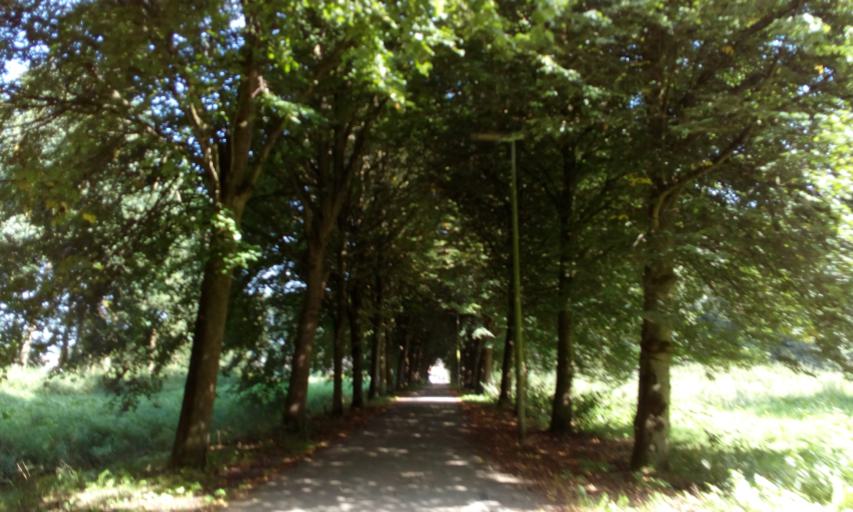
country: NL
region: South Holland
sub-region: Gemeente Waddinxveen
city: Groenswaard
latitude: 52.0629
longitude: 4.6442
